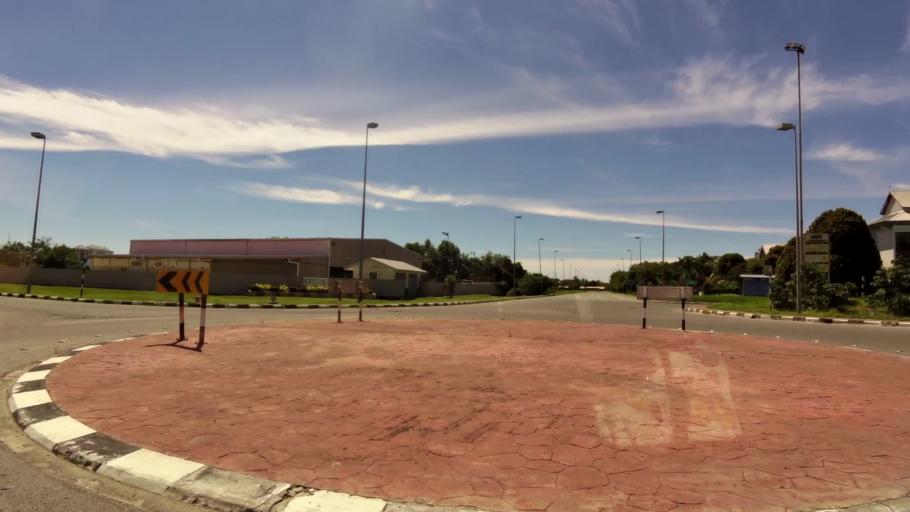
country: BN
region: Brunei and Muara
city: Bandar Seri Begawan
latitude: 5.0285
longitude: 115.0715
